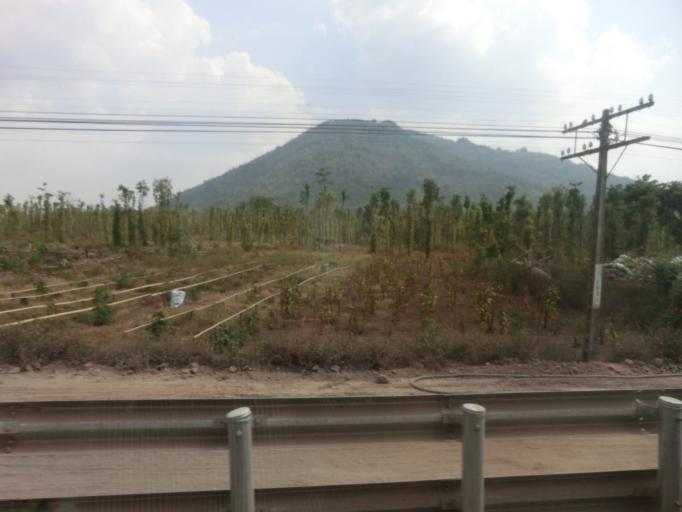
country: VN
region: Dong Nai
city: Gia Ray
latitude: 10.9705
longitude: 107.3886
